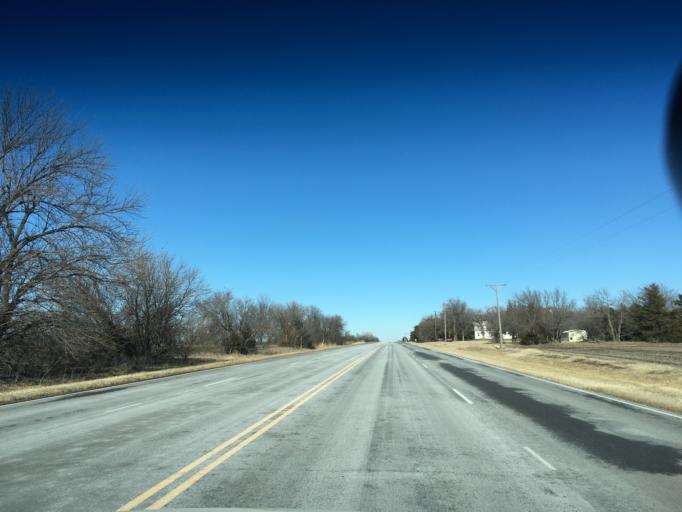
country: US
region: Kansas
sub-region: Harvey County
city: Sedgwick
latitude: 37.9211
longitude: -97.3365
